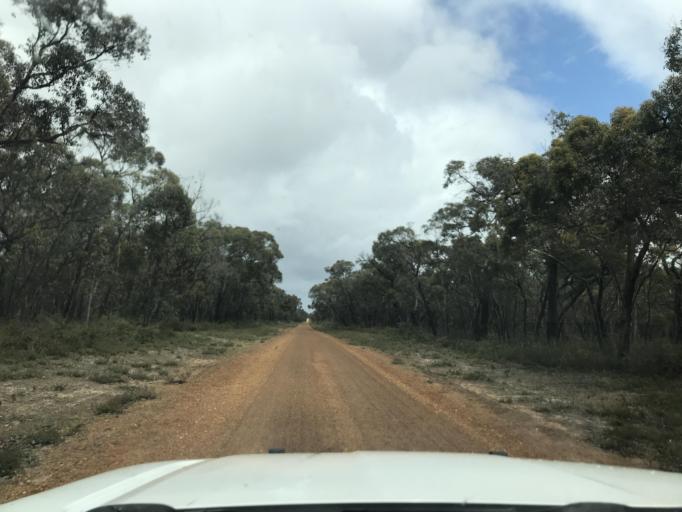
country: AU
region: South Australia
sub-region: Wattle Range
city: Penola
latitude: -37.2939
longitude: 141.3050
